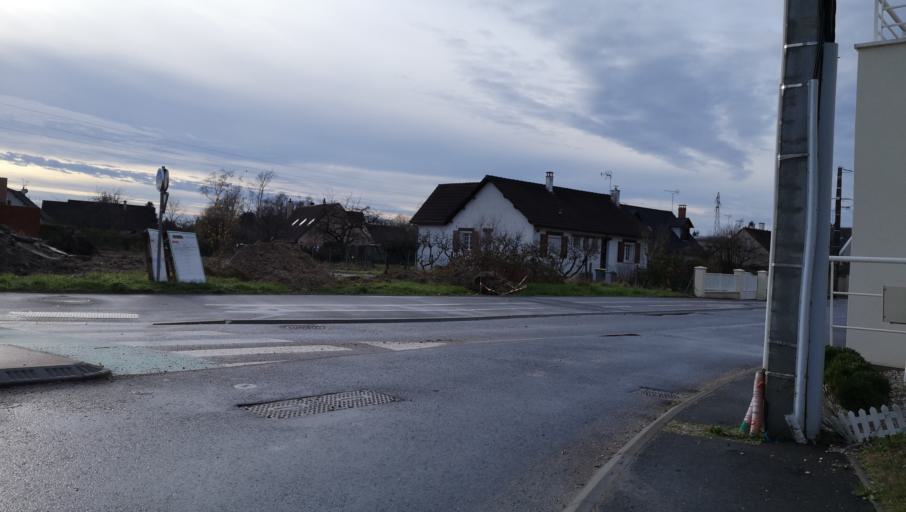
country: FR
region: Centre
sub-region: Departement du Loiret
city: Saint-Jean-de-Braye
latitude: 47.9238
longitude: 1.9708
